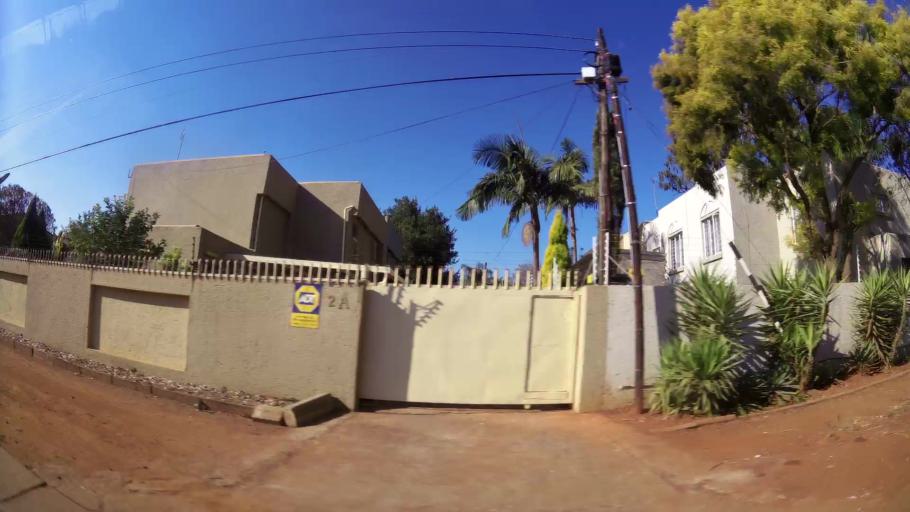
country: ZA
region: Gauteng
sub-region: City of Tshwane Metropolitan Municipality
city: Centurion
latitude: -25.8399
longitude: 28.1785
